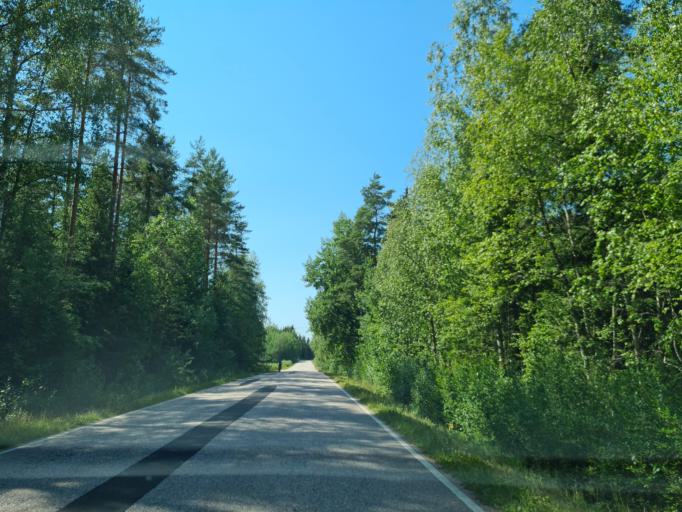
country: FI
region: Varsinais-Suomi
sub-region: Loimaa
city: Aura
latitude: 60.6038
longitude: 22.5932
